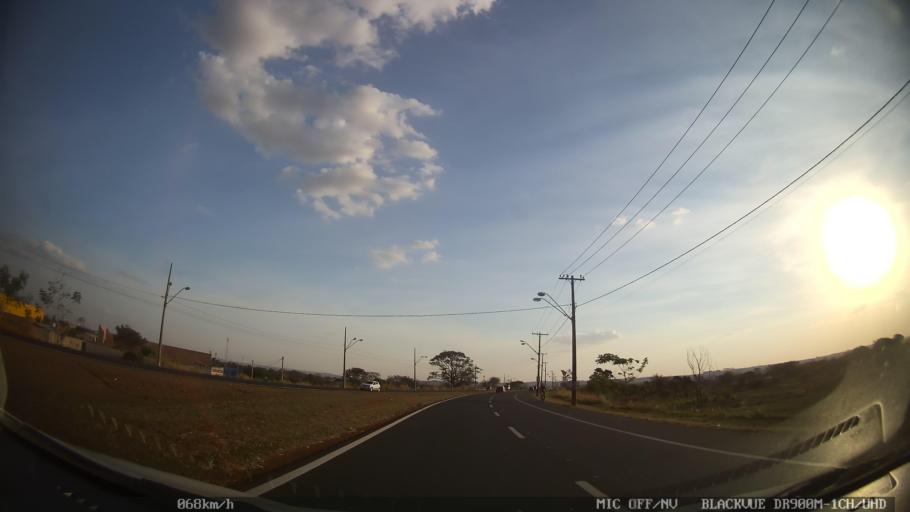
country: BR
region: Sao Paulo
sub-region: Ribeirao Preto
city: Ribeirao Preto
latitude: -21.1290
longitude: -47.7882
